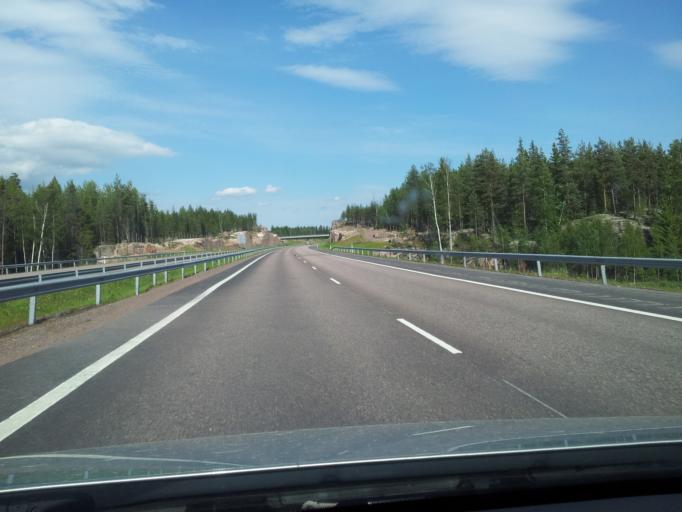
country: FI
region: Uusimaa
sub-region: Loviisa
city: Lovisa
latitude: 60.4841
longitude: 26.2915
